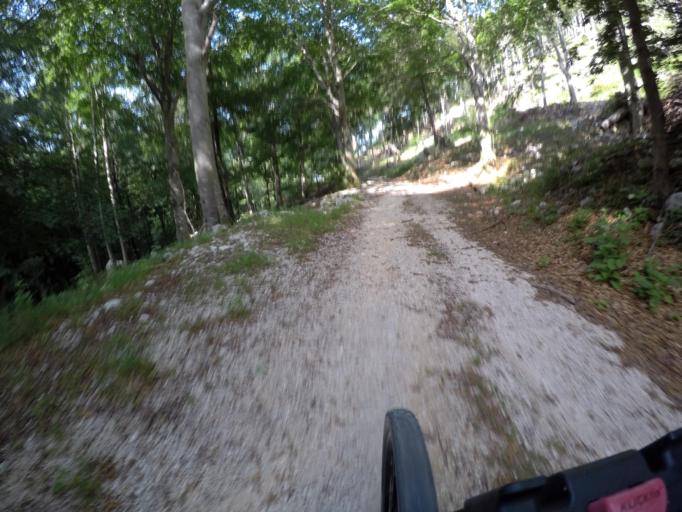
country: IT
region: Friuli Venezia Giulia
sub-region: Provincia di Udine
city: Resiutta
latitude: 46.3337
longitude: 13.2189
